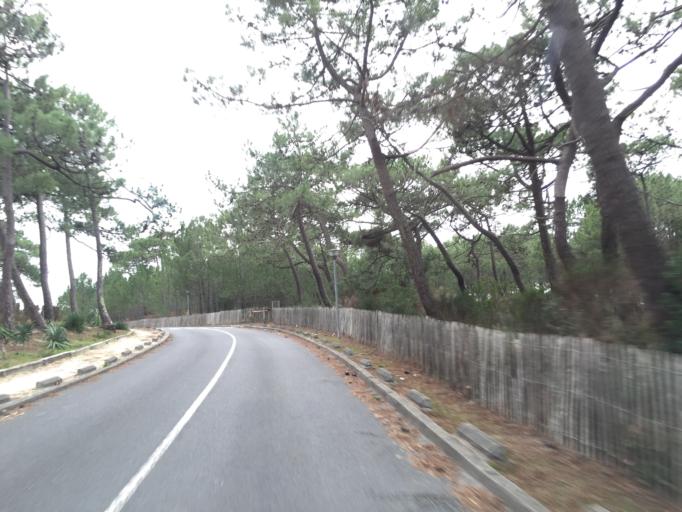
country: FR
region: Aquitaine
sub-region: Departement de la Gironde
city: Lacanau
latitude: 45.0101
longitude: -1.1957
